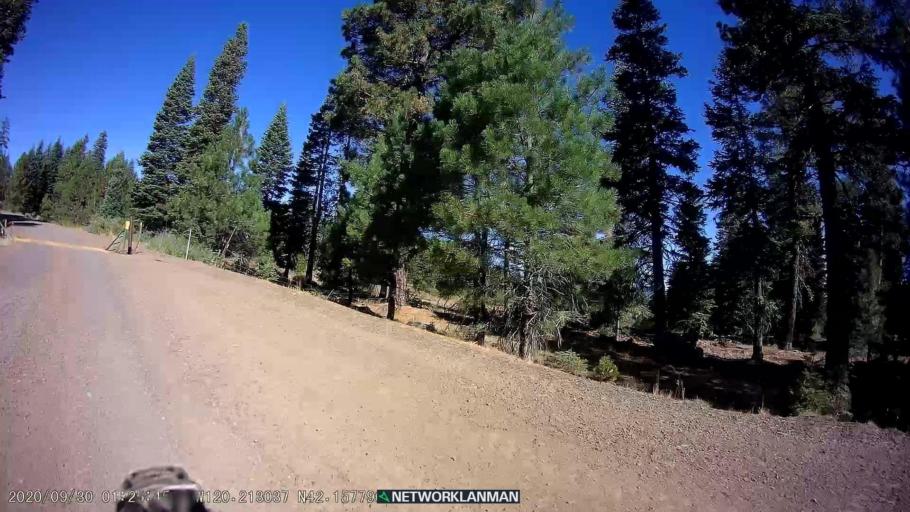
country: US
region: Oregon
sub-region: Lake County
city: Lakeview
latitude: 42.1580
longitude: -120.2176
